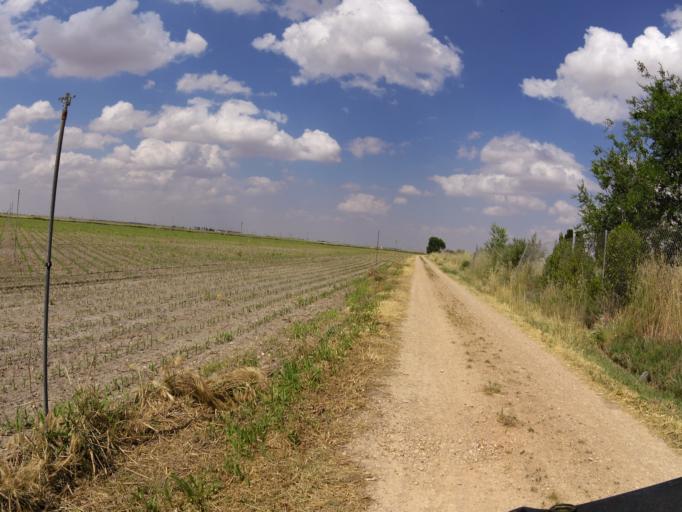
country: ES
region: Castille-La Mancha
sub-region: Provincia de Albacete
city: Pozuelo
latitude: 38.9183
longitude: -2.0091
